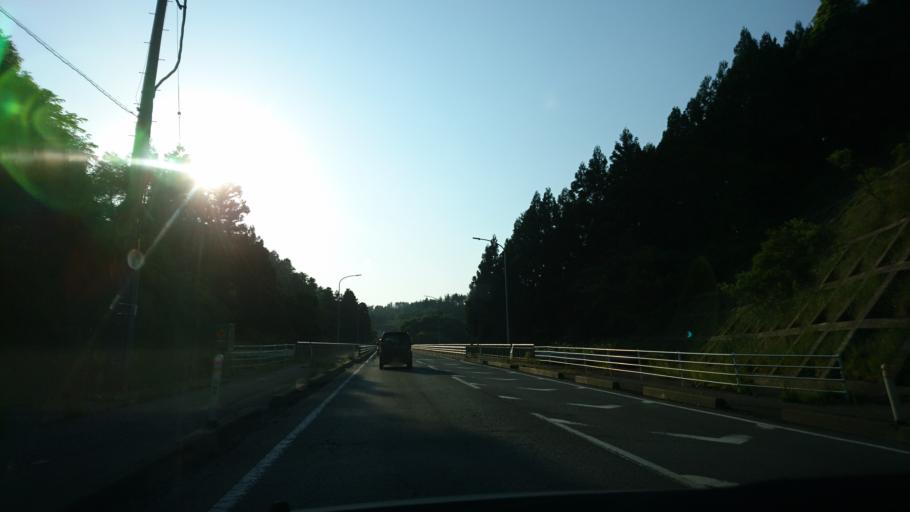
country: JP
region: Iwate
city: Ofunato
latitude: 38.9145
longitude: 141.5251
